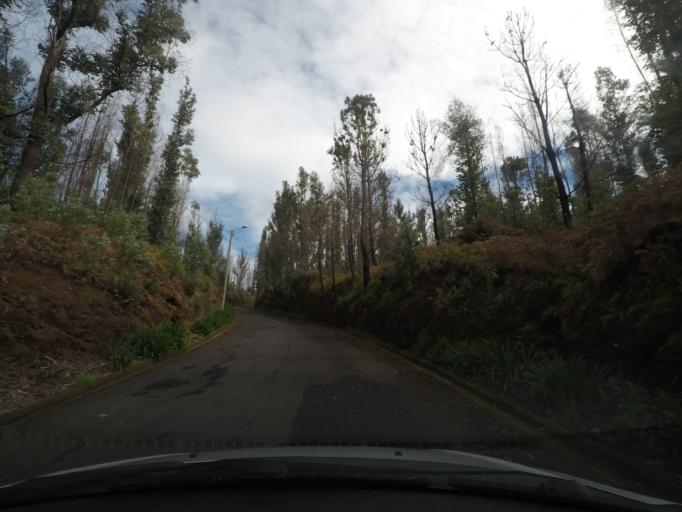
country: PT
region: Madeira
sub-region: Calheta
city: Faja da Ovelha
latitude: 32.8297
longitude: -17.2277
